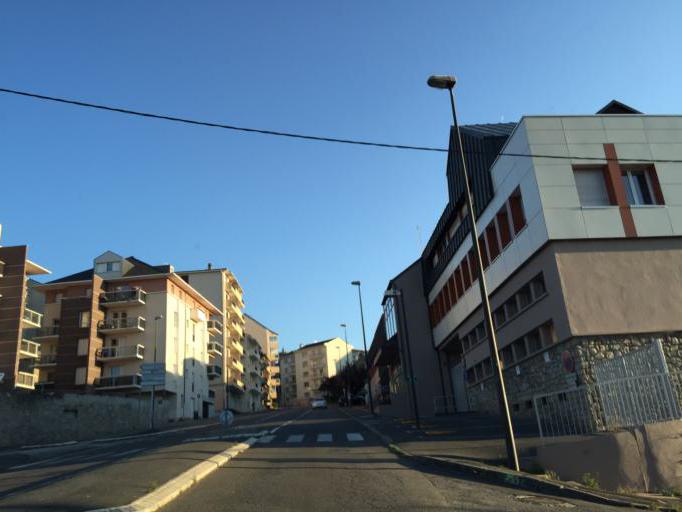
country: FR
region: Midi-Pyrenees
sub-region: Departement de l'Aveyron
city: Rodez
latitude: 44.3582
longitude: 2.5758
